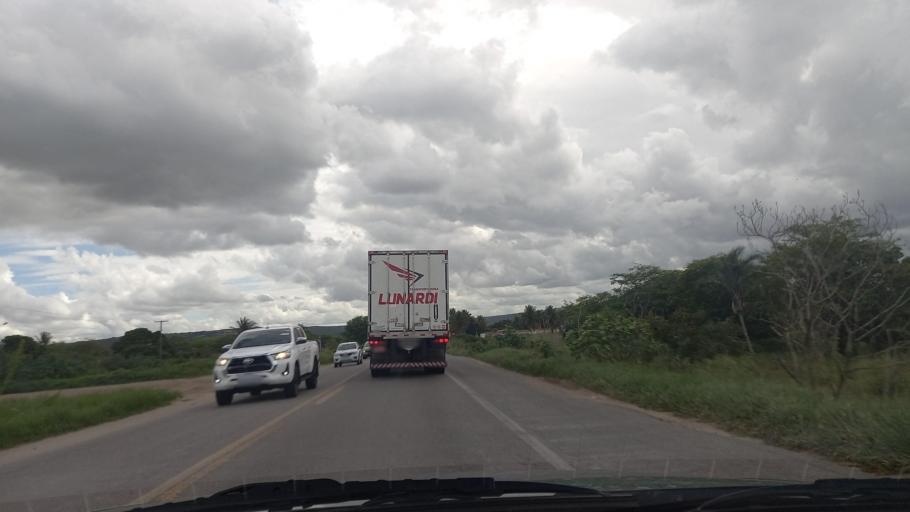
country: BR
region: Pernambuco
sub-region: Lajedo
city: Lajedo
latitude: -8.6615
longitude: -36.3444
